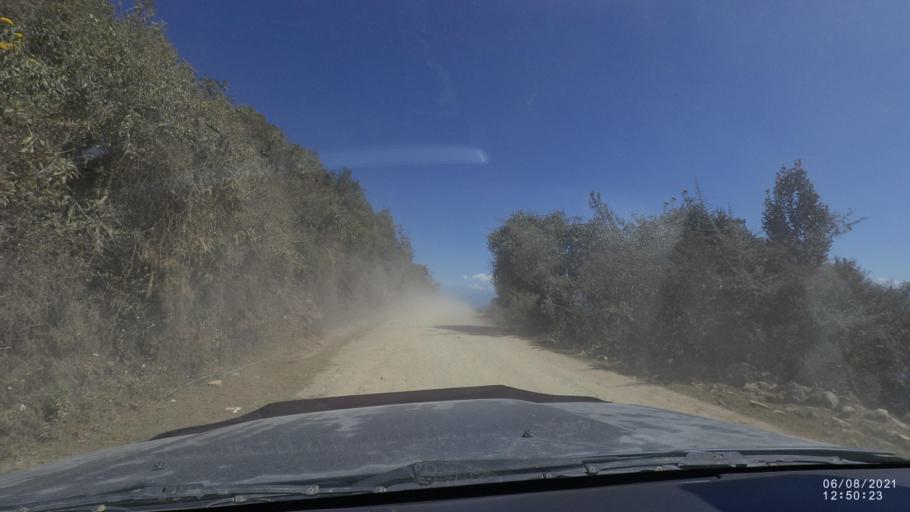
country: BO
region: Cochabamba
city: Colchani
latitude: -16.7599
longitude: -66.6770
